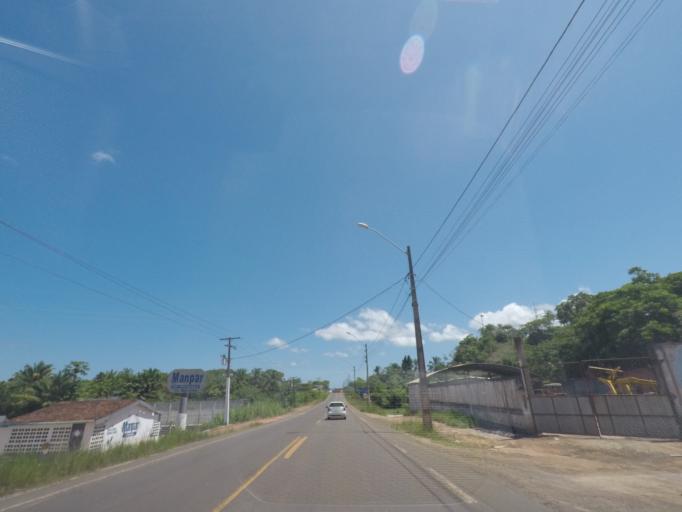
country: BR
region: Bahia
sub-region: Valenca
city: Valenca
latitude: -13.3446
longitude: -39.0633
